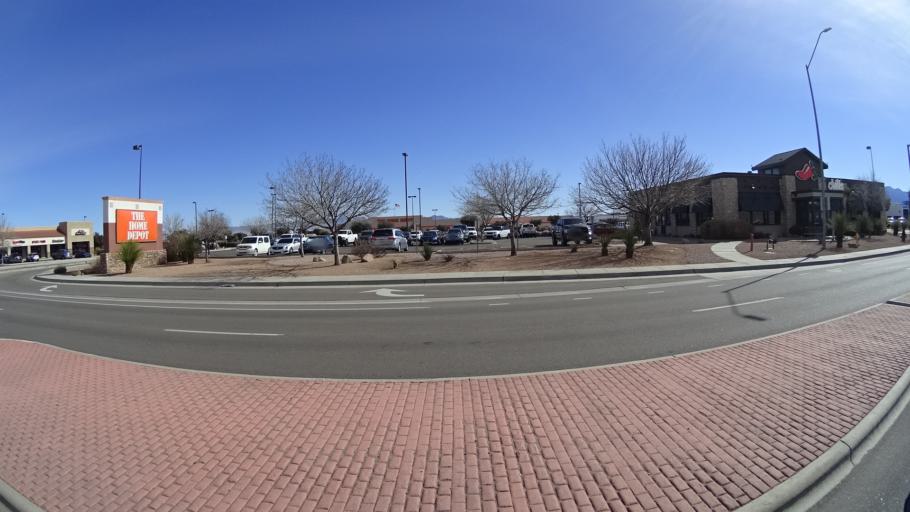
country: US
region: Arizona
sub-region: Mohave County
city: New Kingman-Butler
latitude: 35.2325
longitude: -114.0363
